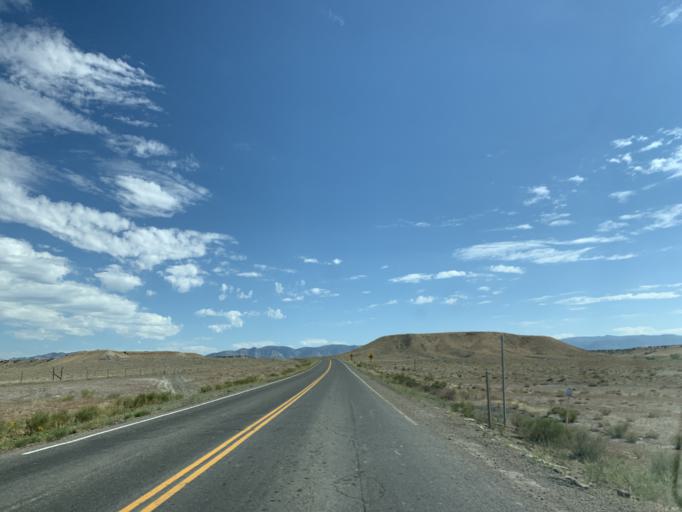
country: US
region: Utah
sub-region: Carbon County
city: Wellington
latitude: 39.5535
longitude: -110.6683
